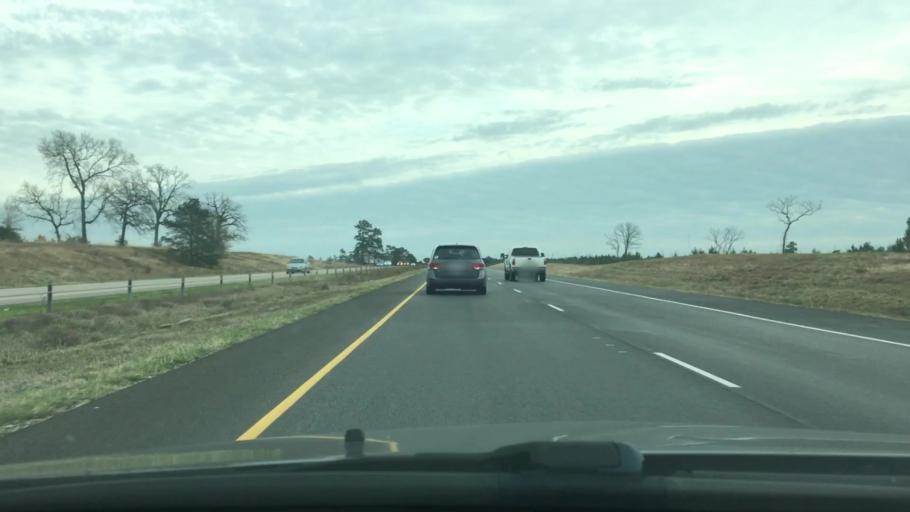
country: US
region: Texas
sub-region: Madison County
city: Madisonville
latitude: 30.8460
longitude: -95.7312
